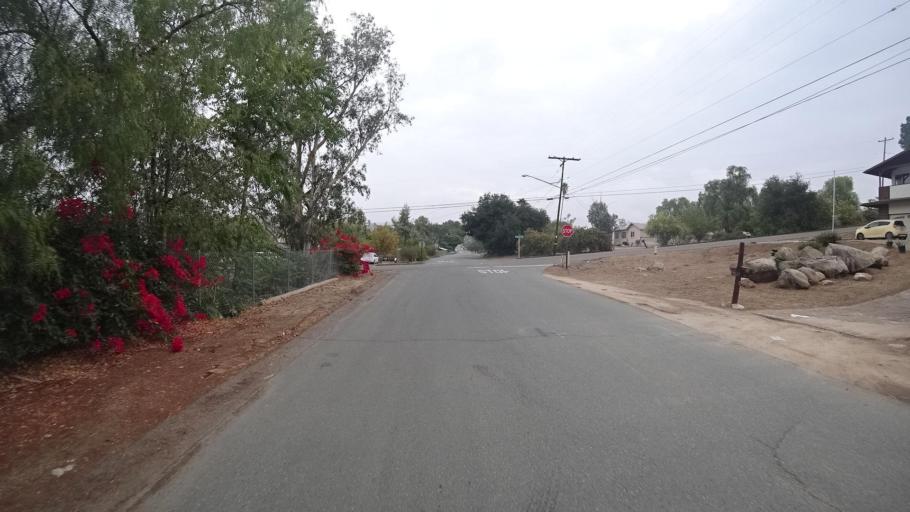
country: US
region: California
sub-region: San Diego County
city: Ramona
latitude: 33.0419
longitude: -116.8599
